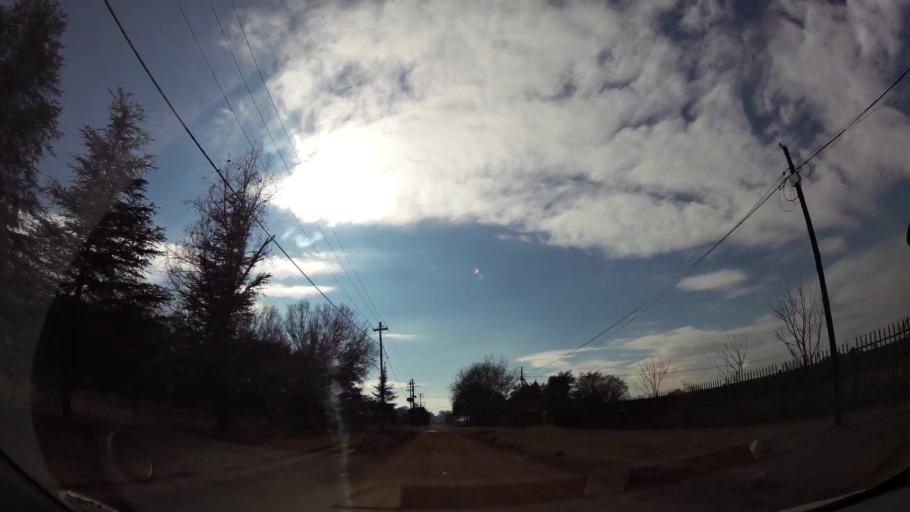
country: ZA
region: Gauteng
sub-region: Sedibeng District Municipality
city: Meyerton
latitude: -26.5526
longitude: 28.0542
